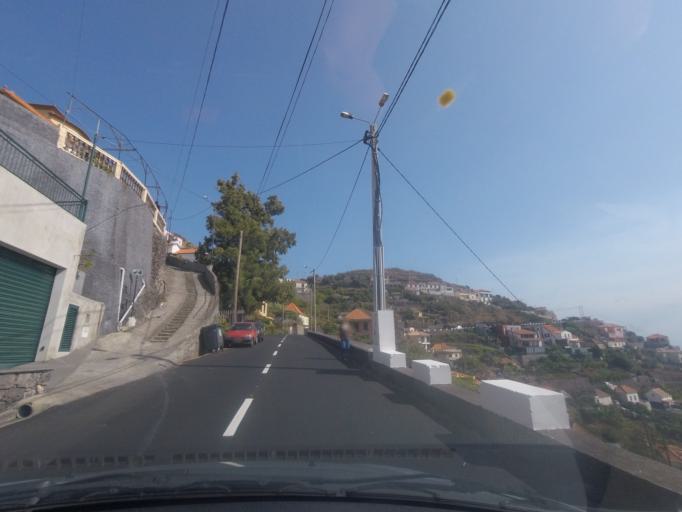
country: PT
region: Madeira
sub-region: Ribeira Brava
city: Campanario
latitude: 32.6695
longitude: -17.0382
